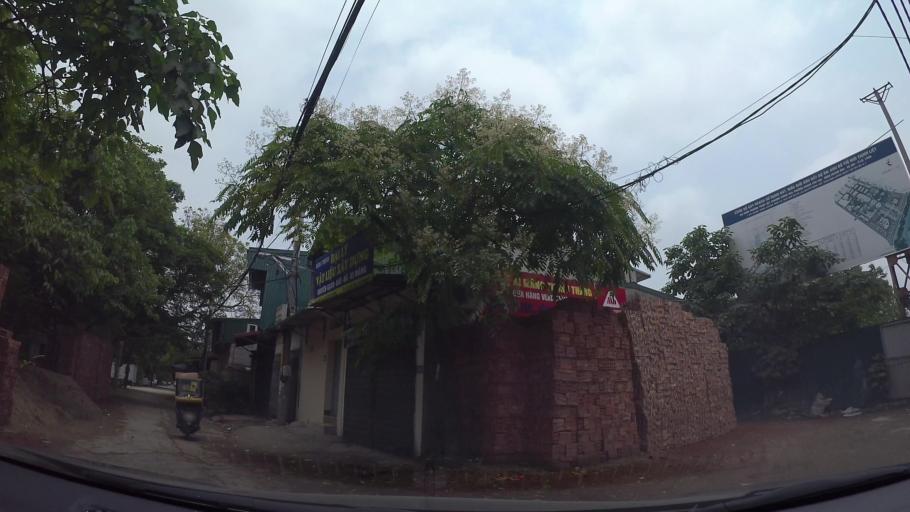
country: VN
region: Ha Noi
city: Van Dien
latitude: 20.9770
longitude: 105.8535
